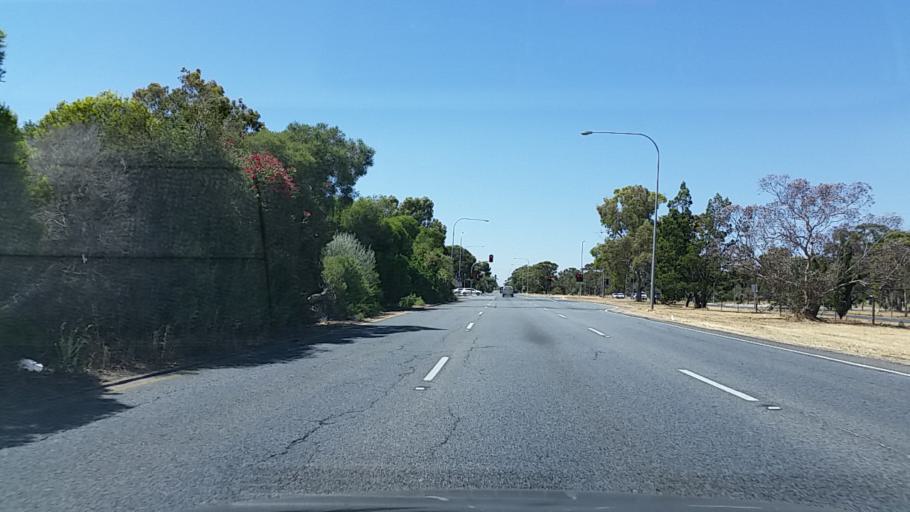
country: AU
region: South Australia
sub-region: Playford
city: Smithfield
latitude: -34.7007
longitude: 138.6824
